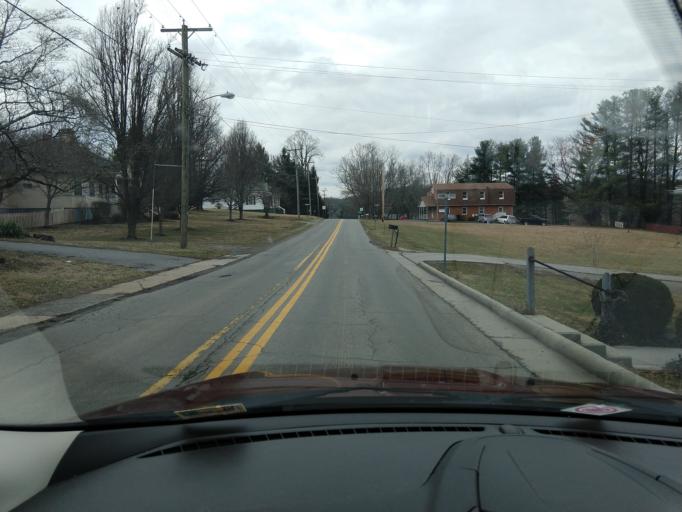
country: US
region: Virginia
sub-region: Floyd County
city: Floyd
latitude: 36.9130
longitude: -80.3169
